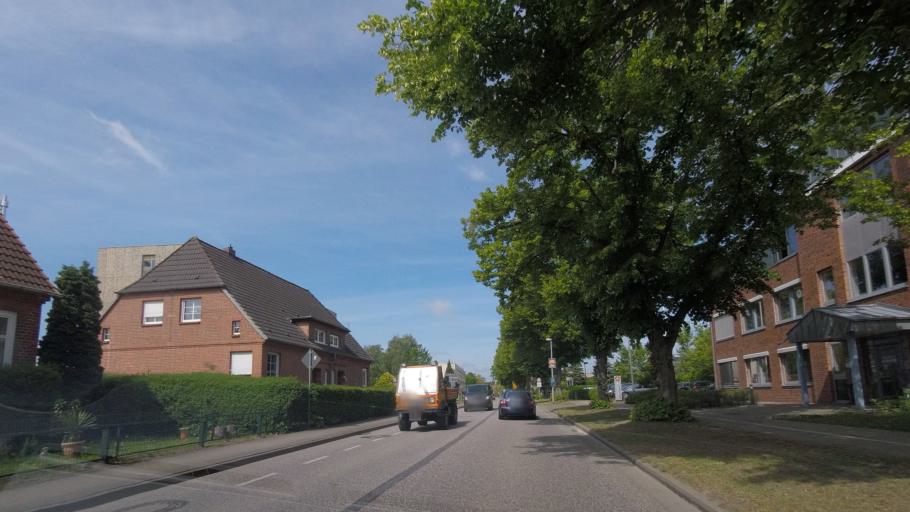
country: DE
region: Brandenburg
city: Wittstock
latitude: 53.1629
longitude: 12.4968
